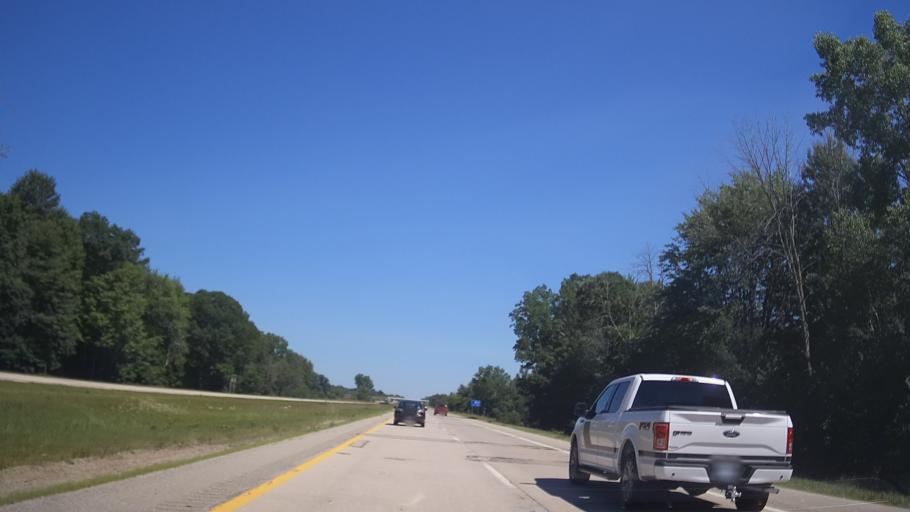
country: US
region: Michigan
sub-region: Clare County
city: Clare
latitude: 43.8046
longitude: -84.6809
